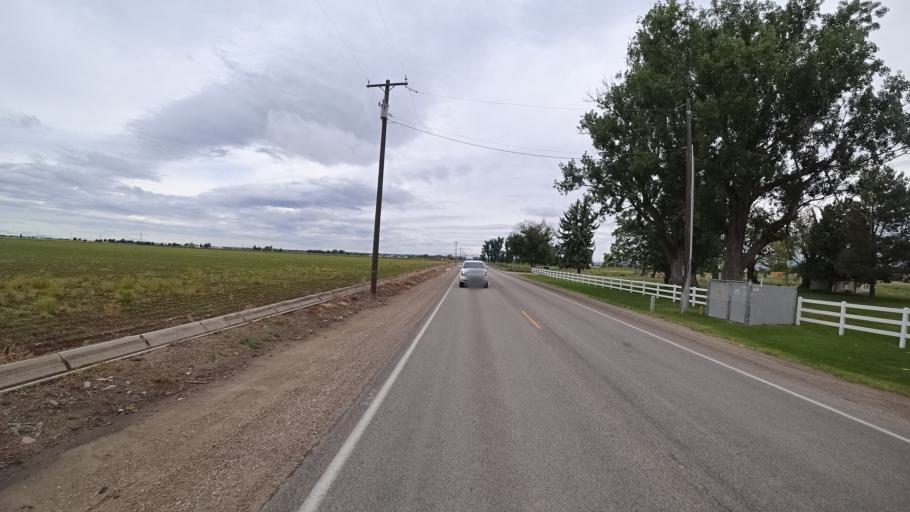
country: US
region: Idaho
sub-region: Ada County
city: Star
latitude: 43.6525
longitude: -116.4936
